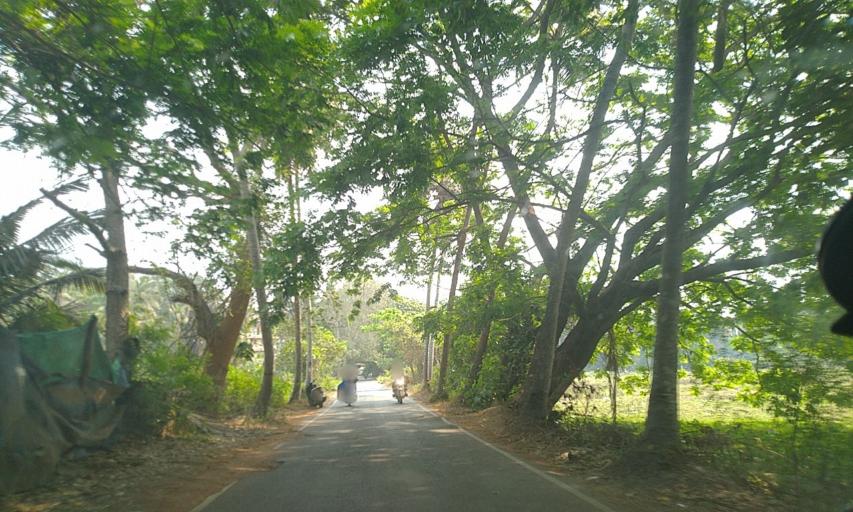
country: IN
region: Goa
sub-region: North Goa
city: Taleigao
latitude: 15.4738
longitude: 73.8423
